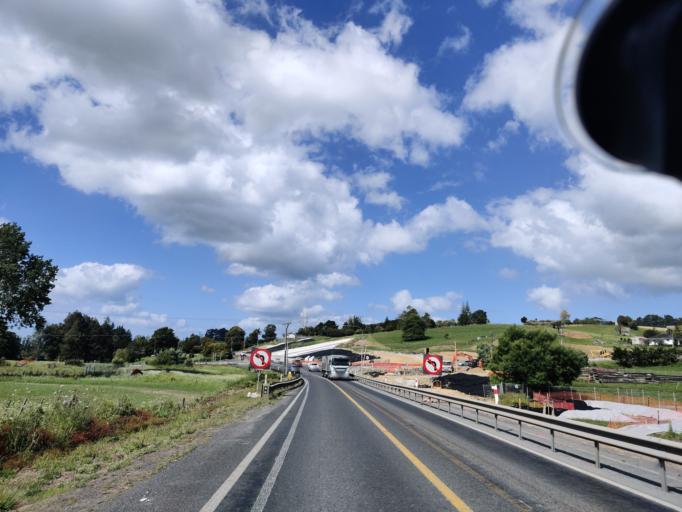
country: NZ
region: Northland
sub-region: Whangarei
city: Whangarei
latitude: -35.7905
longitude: 174.3013
